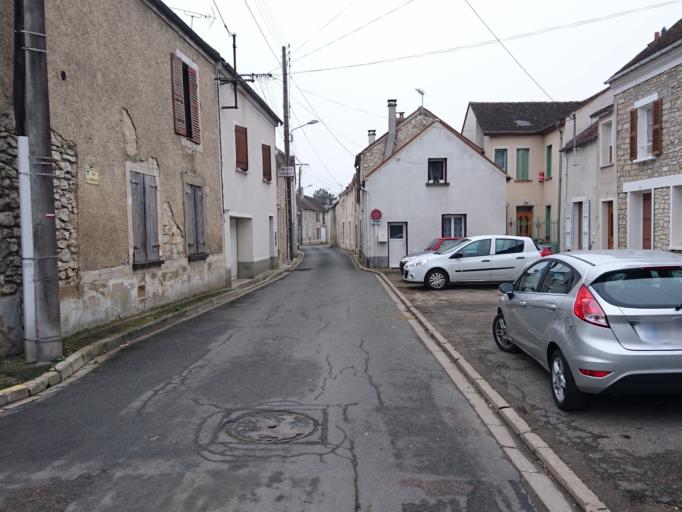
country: FR
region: Ile-de-France
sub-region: Departement de Seine-et-Marne
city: Veneux-les-Sablons
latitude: 48.3759
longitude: 2.7928
